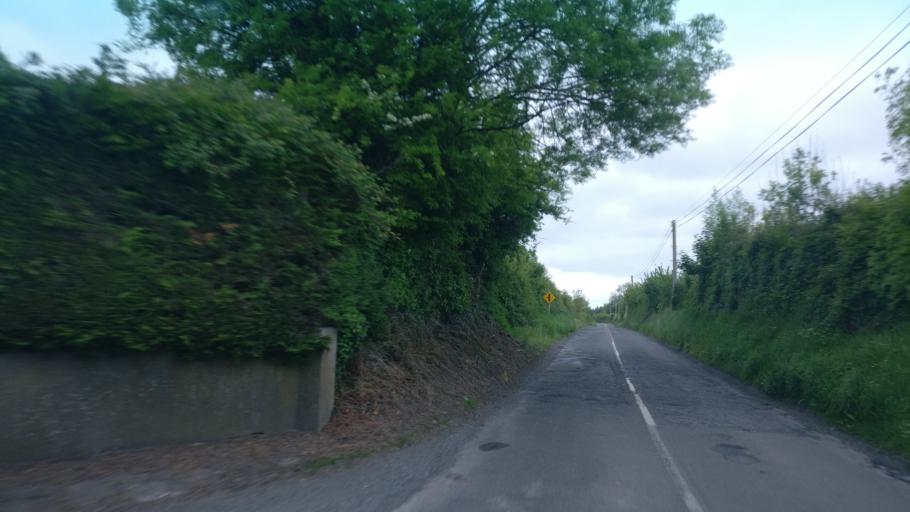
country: IE
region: Connaught
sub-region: County Galway
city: Portumna
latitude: 53.1034
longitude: -8.2559
